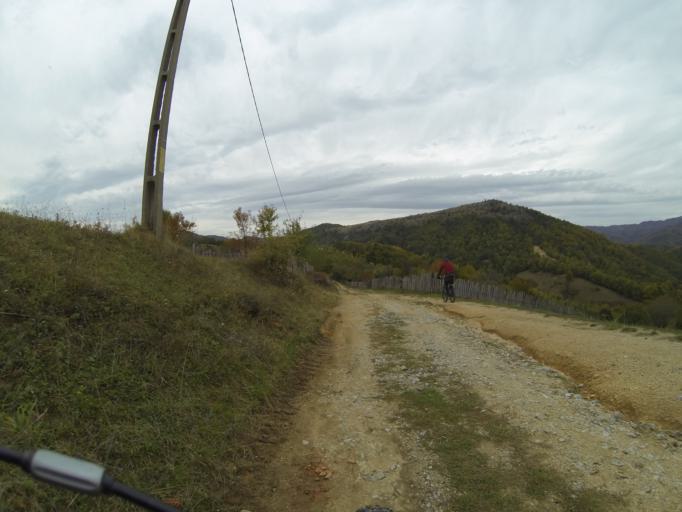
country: RO
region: Gorj
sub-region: Comuna Tismana
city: Sohodol
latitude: 45.0576
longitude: 22.8925
